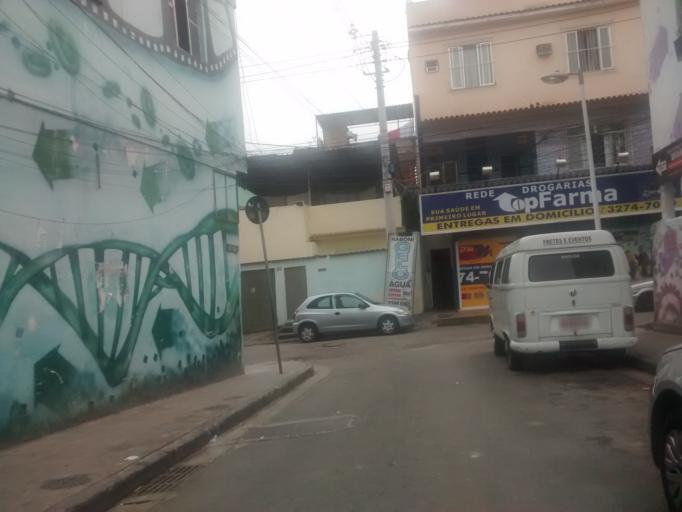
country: BR
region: Rio de Janeiro
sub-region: Rio De Janeiro
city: Rio de Janeiro
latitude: -22.8655
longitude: -43.2732
